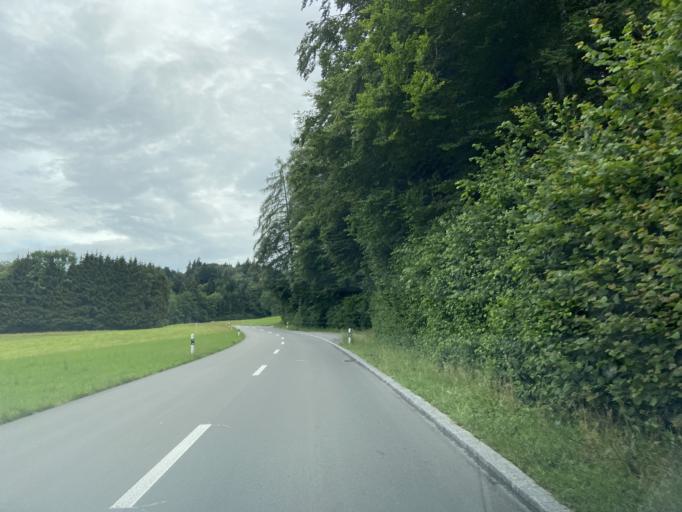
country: CH
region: Thurgau
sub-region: Muenchwilen District
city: Aadorf
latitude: 47.4689
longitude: 8.8907
